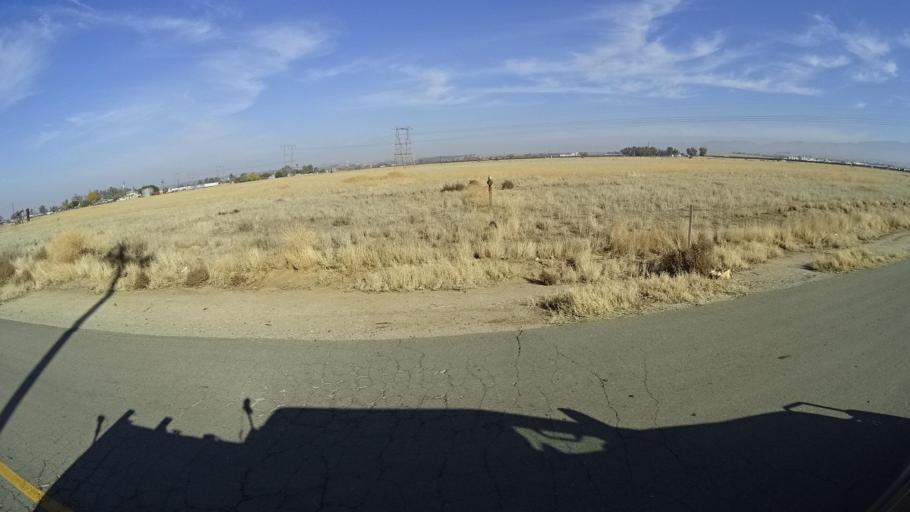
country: US
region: California
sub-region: Kern County
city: Lamont
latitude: 35.3398
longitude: -118.9033
